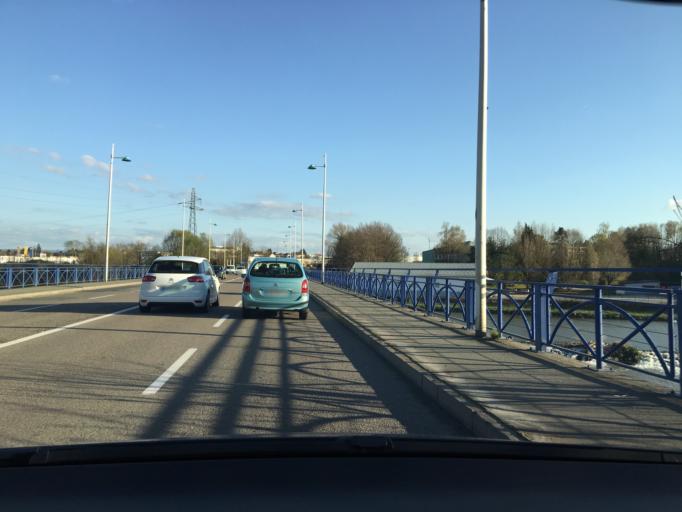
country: FR
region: Franche-Comte
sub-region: Departement du Doubs
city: Montbeliard
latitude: 47.5056
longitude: 6.8107
